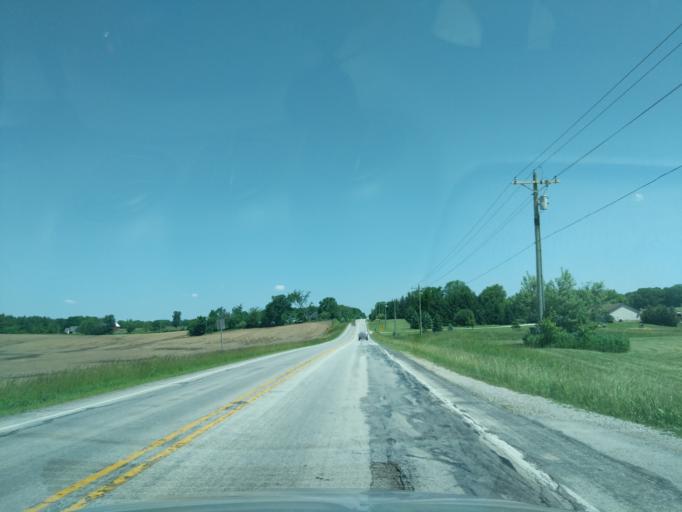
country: US
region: Indiana
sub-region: Whitley County
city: Tri-Lakes
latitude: 41.2182
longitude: -85.4919
